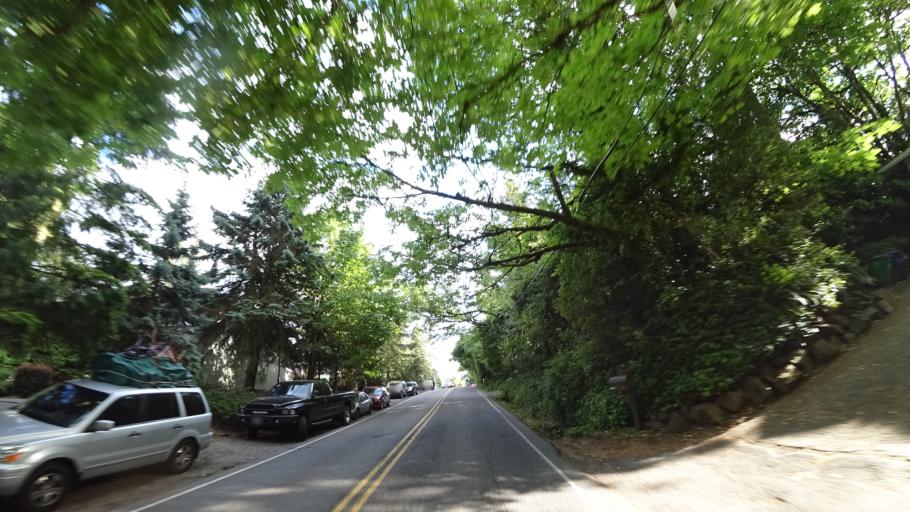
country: US
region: Oregon
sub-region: Washington County
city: Garden Home-Whitford
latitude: 45.4691
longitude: -122.7231
